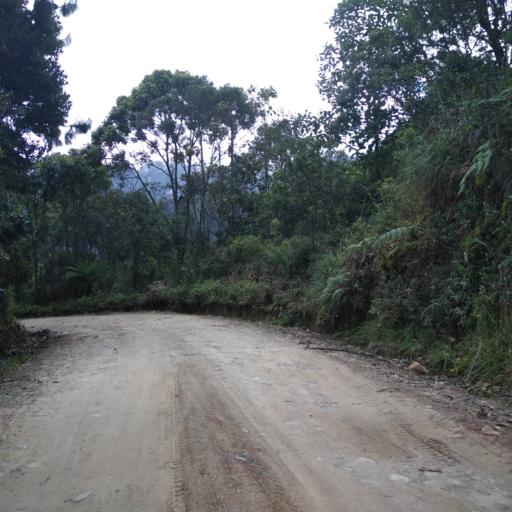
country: CO
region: Boyaca
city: Duitama
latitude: 5.9491
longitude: -73.1455
